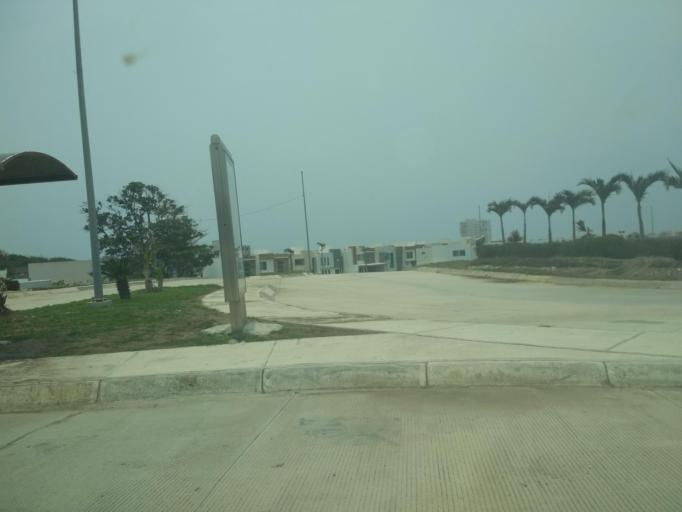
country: MX
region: Veracruz
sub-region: Alvarado
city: Playa de la Libertad
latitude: 19.0572
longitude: -96.0654
